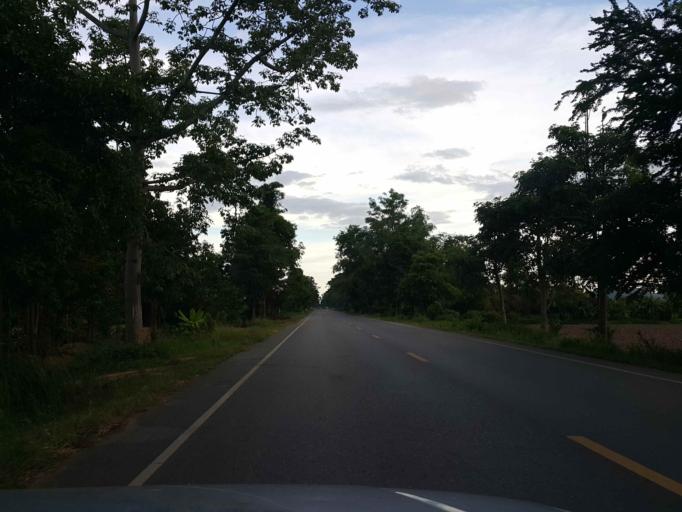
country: TH
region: Sukhothai
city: Sawankhalok
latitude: 17.3572
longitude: 99.7421
